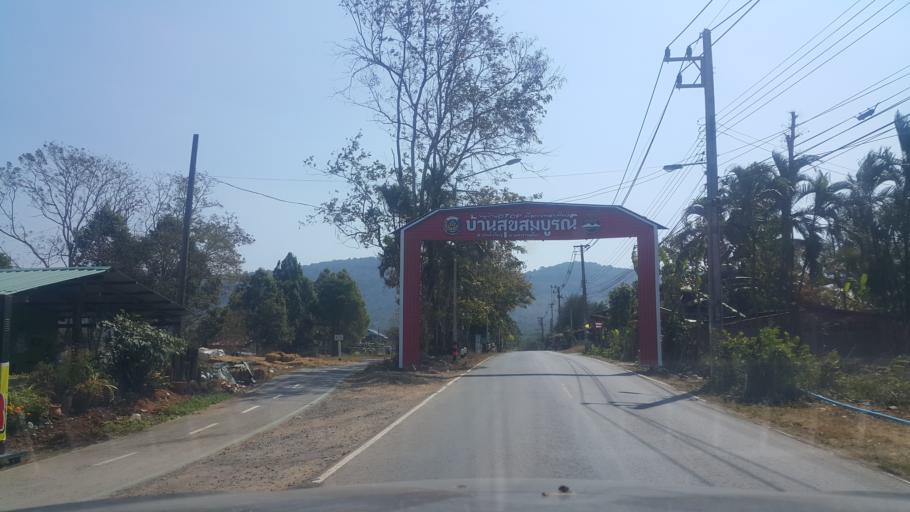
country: TH
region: Nakhon Ratchasima
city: Wang Nam Khiao
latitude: 14.3482
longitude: 101.9396
